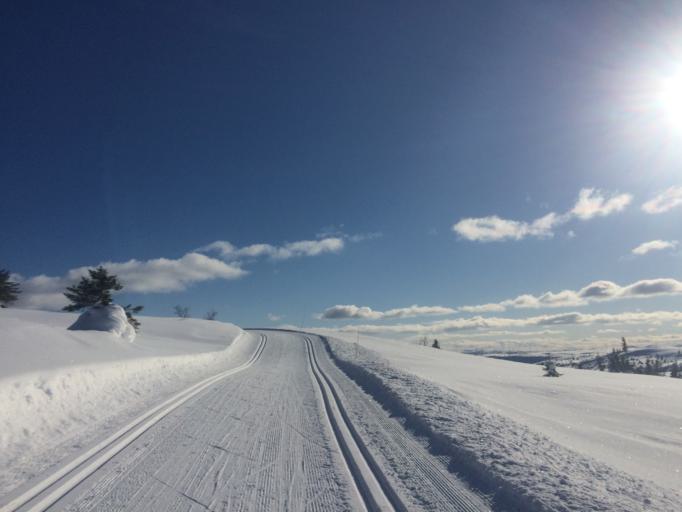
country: NO
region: Oppland
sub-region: Ringebu
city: Ringebu
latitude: 61.3734
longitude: 10.0601
